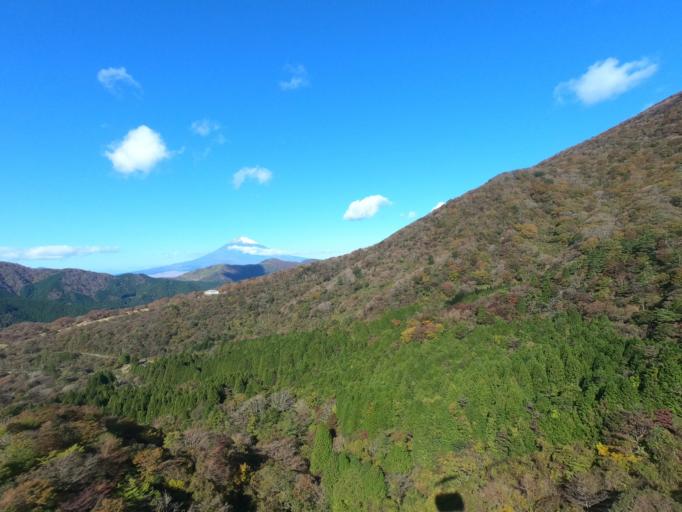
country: JP
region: Kanagawa
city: Hakone
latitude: 35.2175
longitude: 139.0157
